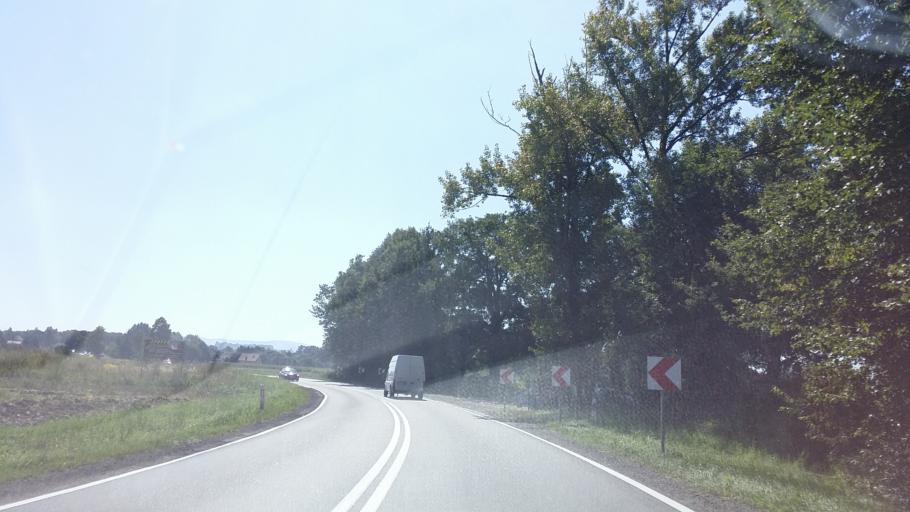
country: PL
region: Lesser Poland Voivodeship
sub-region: Powiat oswiecimski
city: Zator
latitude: 49.9673
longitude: 19.4407
